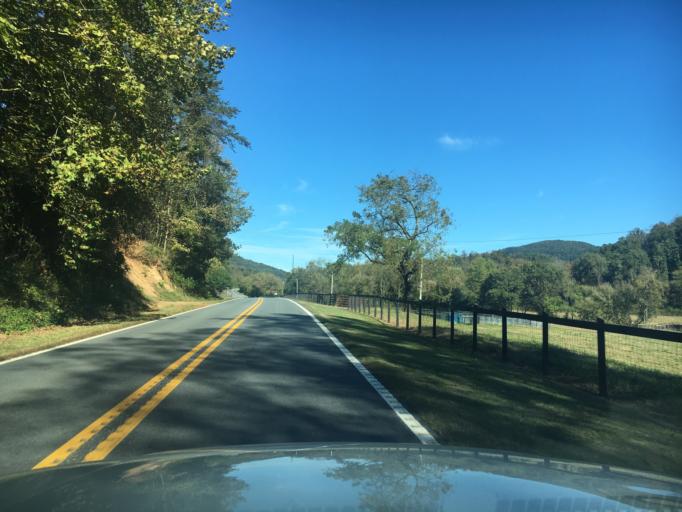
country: US
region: North Carolina
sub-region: Rutherford County
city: Spindale
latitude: 35.5240
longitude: -81.8552
